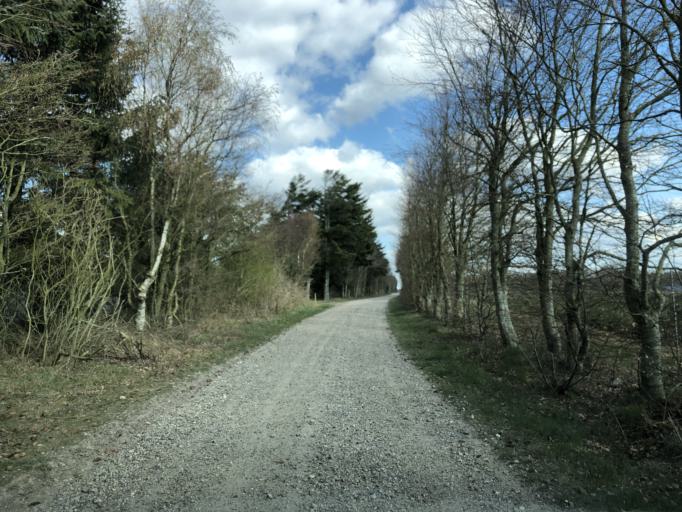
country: DK
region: Central Jutland
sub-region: Holstebro Kommune
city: Ulfborg
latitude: 56.3840
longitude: 8.2098
